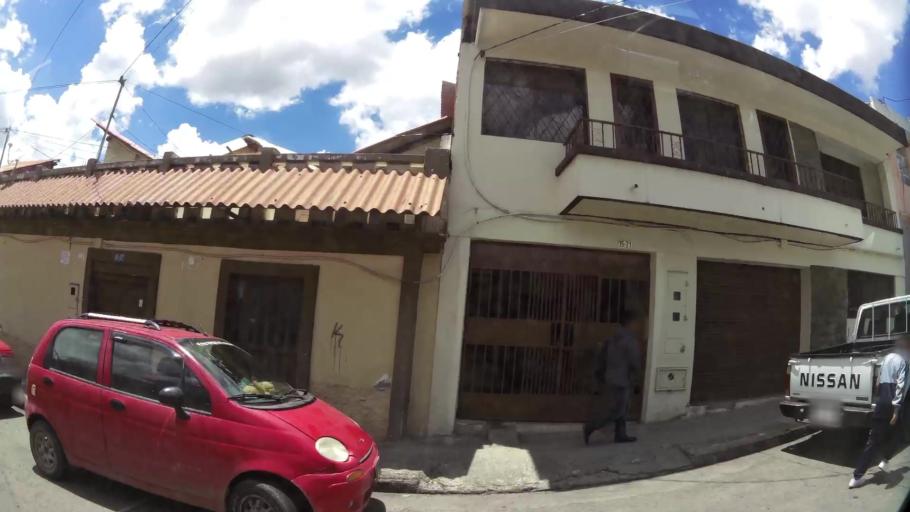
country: EC
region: Azuay
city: Cuenca
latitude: -2.8905
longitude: -79.0028
